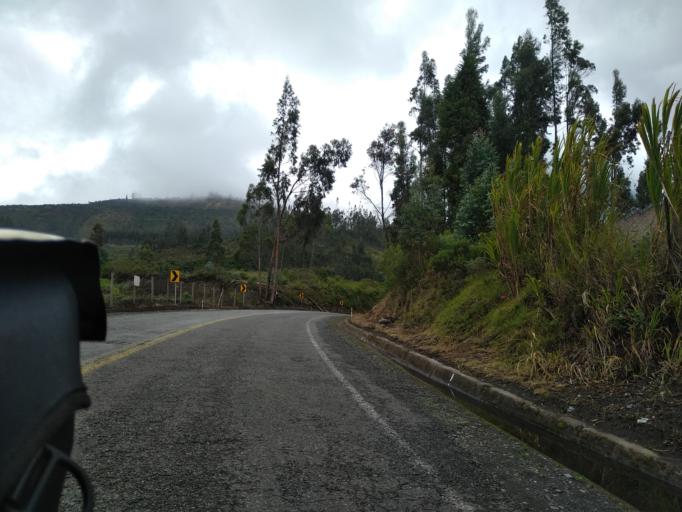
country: EC
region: Chimborazo
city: Guano
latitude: -1.5223
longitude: -78.5133
